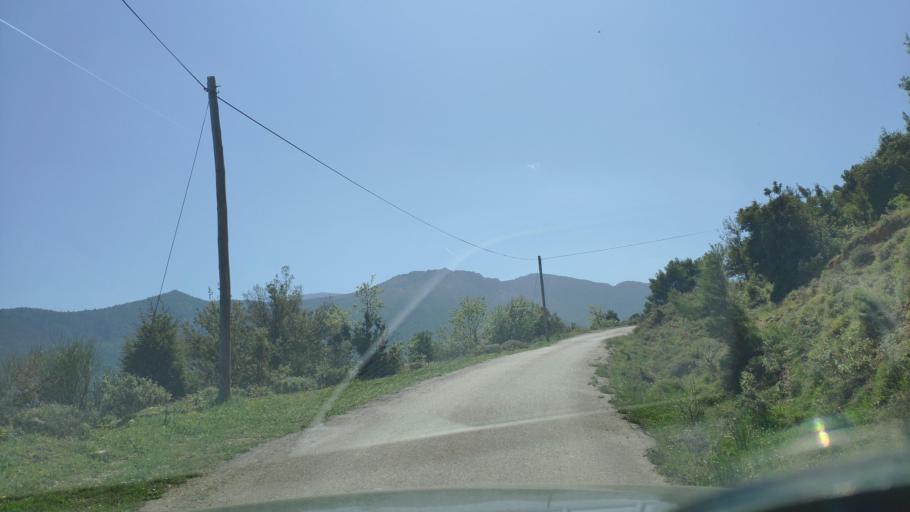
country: GR
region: West Greece
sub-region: Nomos Achaias
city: Akrata
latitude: 38.0810
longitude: 22.3235
